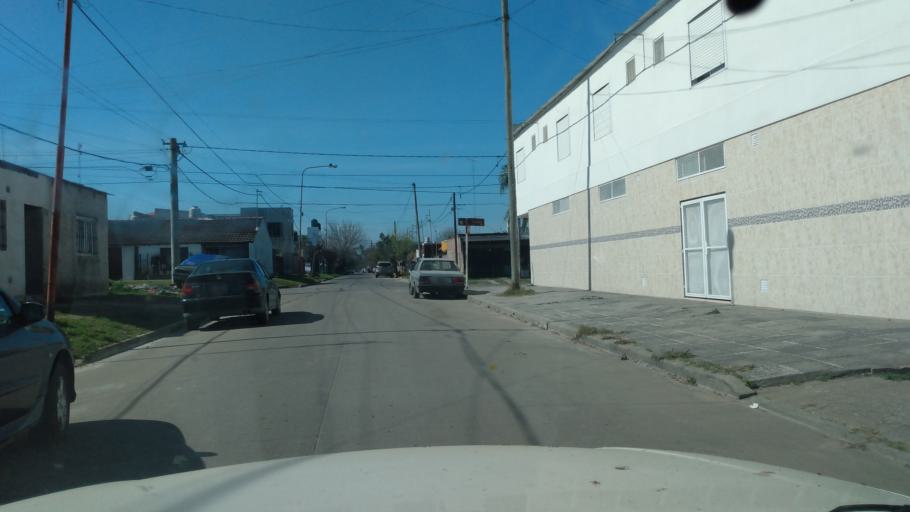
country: AR
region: Buenos Aires
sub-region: Partido de Lujan
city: Lujan
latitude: -34.5836
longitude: -59.1078
